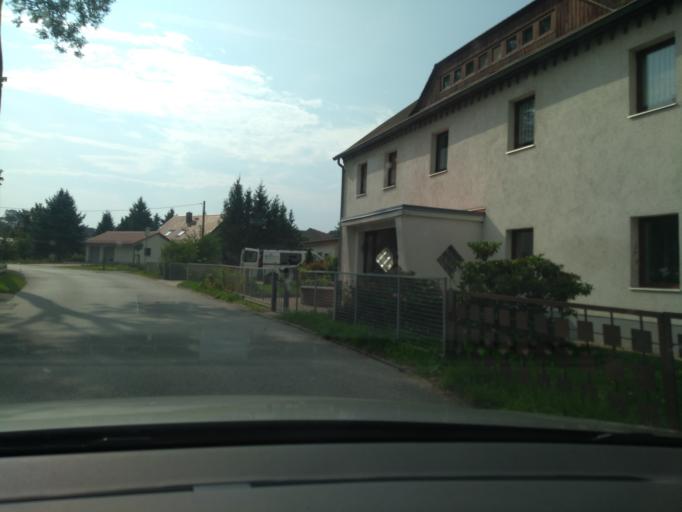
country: DE
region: Saxony
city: Markersdorf
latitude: 51.1383
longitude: 14.8771
